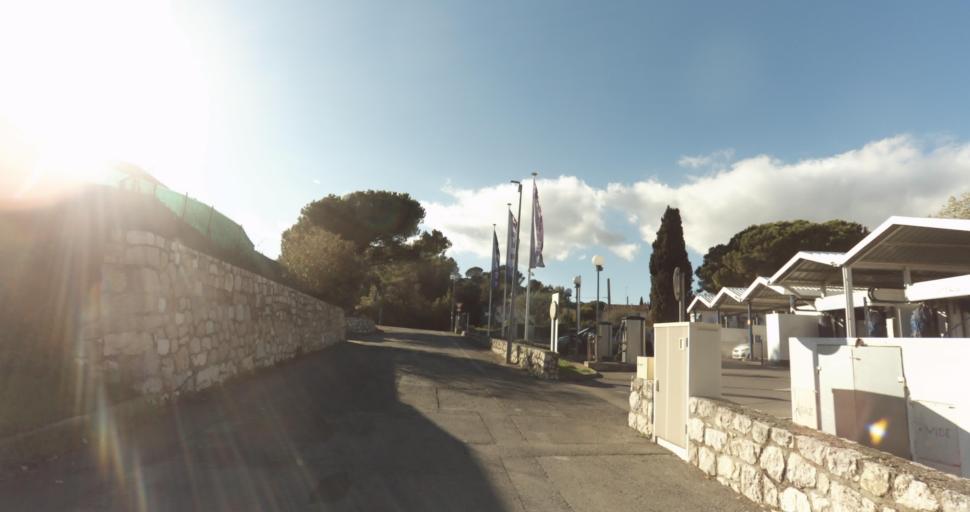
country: FR
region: Provence-Alpes-Cote d'Azur
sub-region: Departement des Alpes-Maritimes
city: Saint-Paul-de-Vence
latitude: 43.7052
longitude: 7.1337
